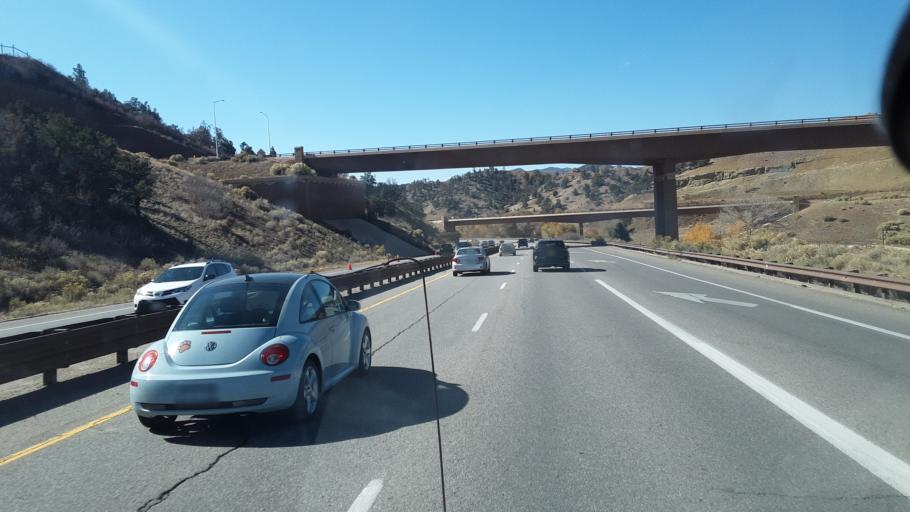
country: US
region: Colorado
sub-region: La Plata County
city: Durango
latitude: 37.2278
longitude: -107.8381
